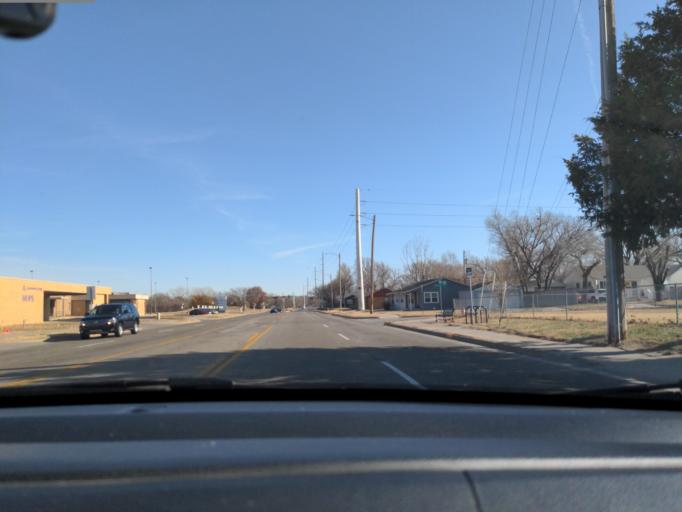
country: US
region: Kansas
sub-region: Sedgwick County
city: Wichita
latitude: 37.6948
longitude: -97.3742
